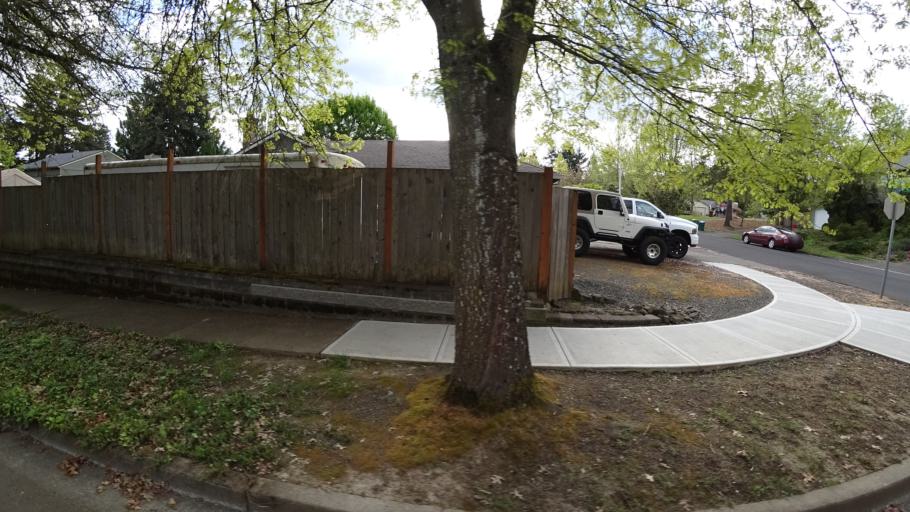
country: US
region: Oregon
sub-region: Washington County
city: Beaverton
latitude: 45.4496
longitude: -122.8209
